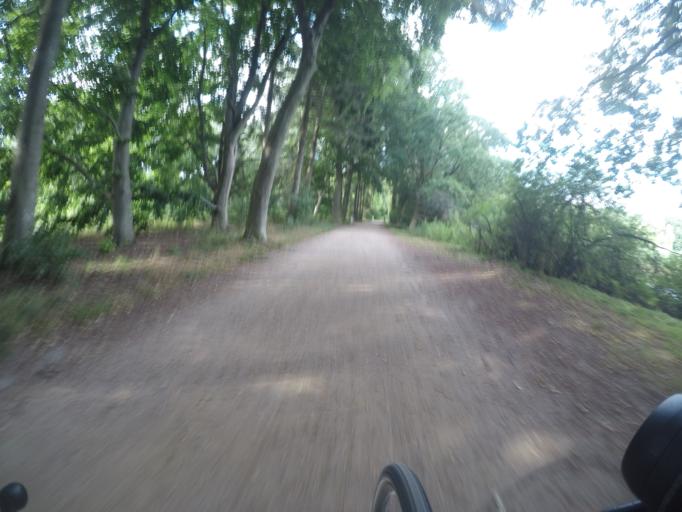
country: DE
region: Schleswig-Holstein
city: Barsbuettel
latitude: 53.5633
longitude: 10.1381
